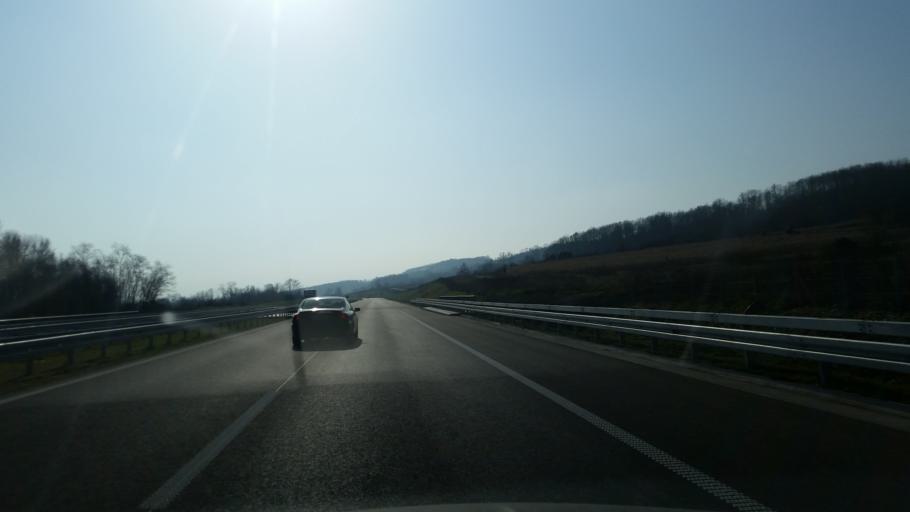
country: RS
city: Prislonica
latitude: 43.9489
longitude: 20.4005
